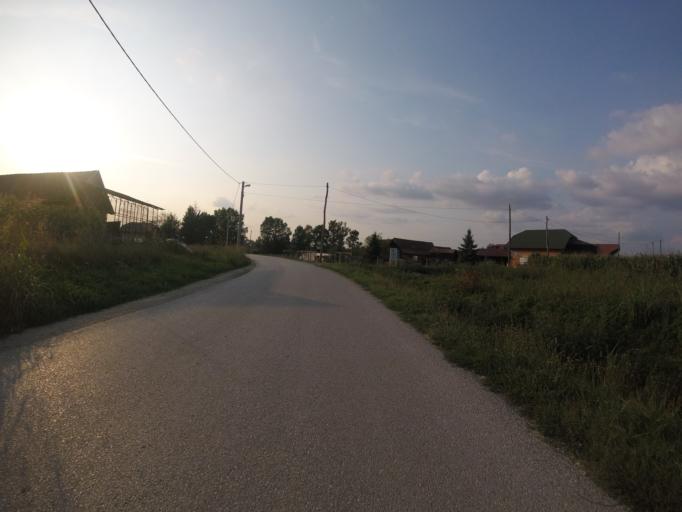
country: HR
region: Zagrebacka
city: Kuce
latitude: 45.7272
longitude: 16.2029
